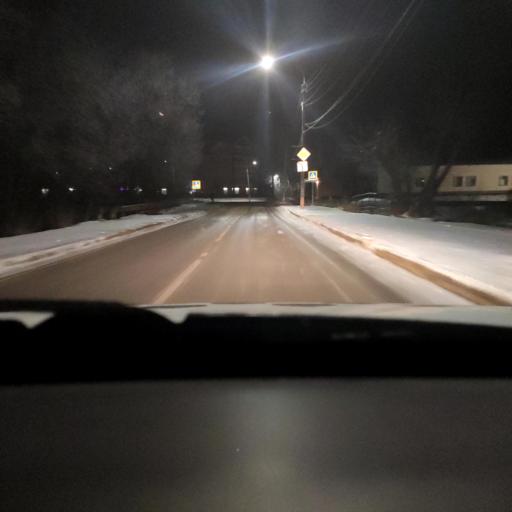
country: RU
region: Perm
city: Ust'-Kachka
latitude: 58.0040
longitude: 55.6739
